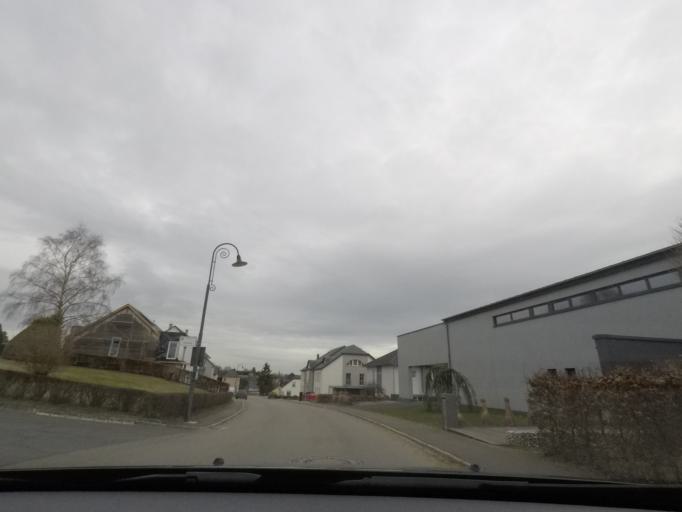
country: LU
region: Diekirch
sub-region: Canton de Clervaux
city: Wincrange
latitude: 50.0190
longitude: 5.9033
